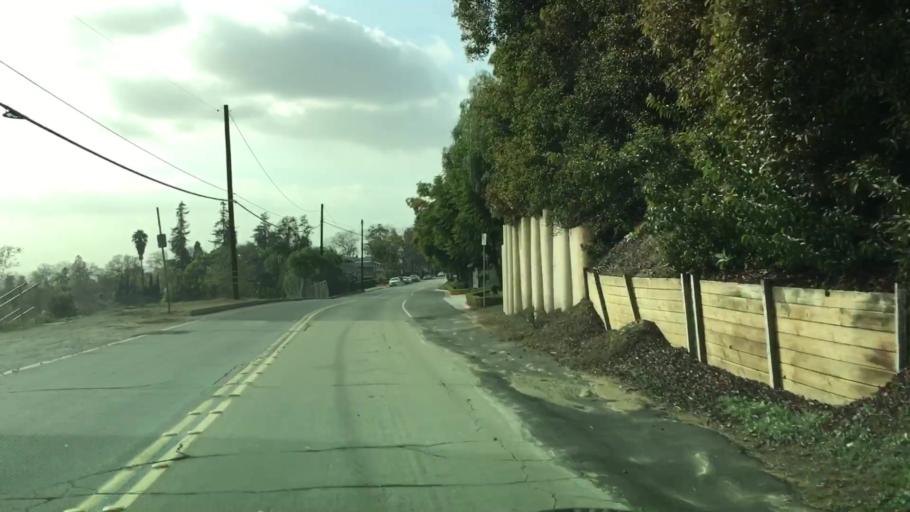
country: US
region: California
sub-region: Los Angeles County
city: Whittier
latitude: 33.9883
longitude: -118.0271
